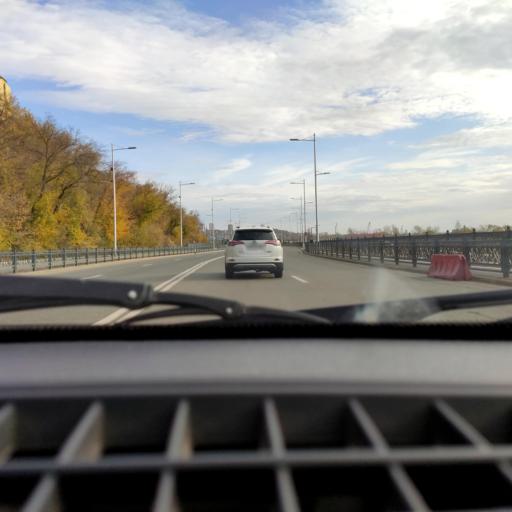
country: RU
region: Bashkortostan
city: Ufa
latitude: 54.7142
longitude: 55.9374
